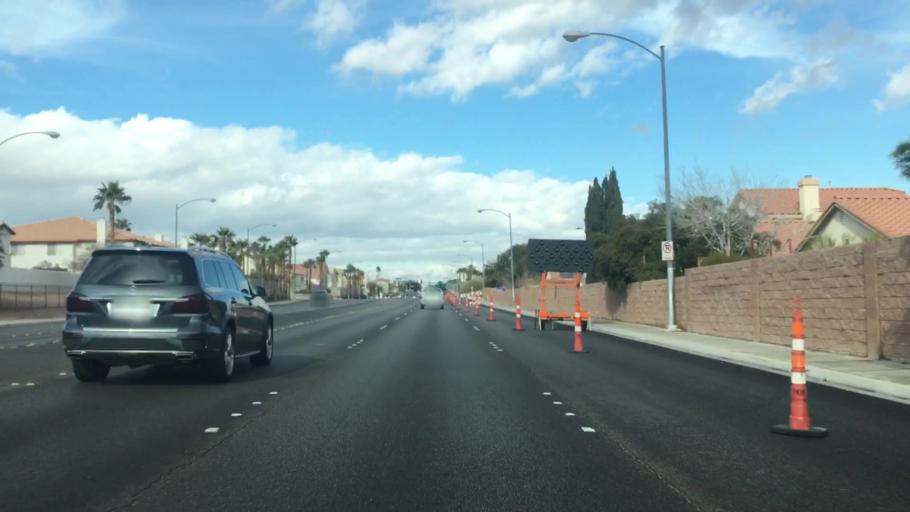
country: US
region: Nevada
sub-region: Clark County
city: Summerlin South
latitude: 36.1192
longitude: -115.2969
